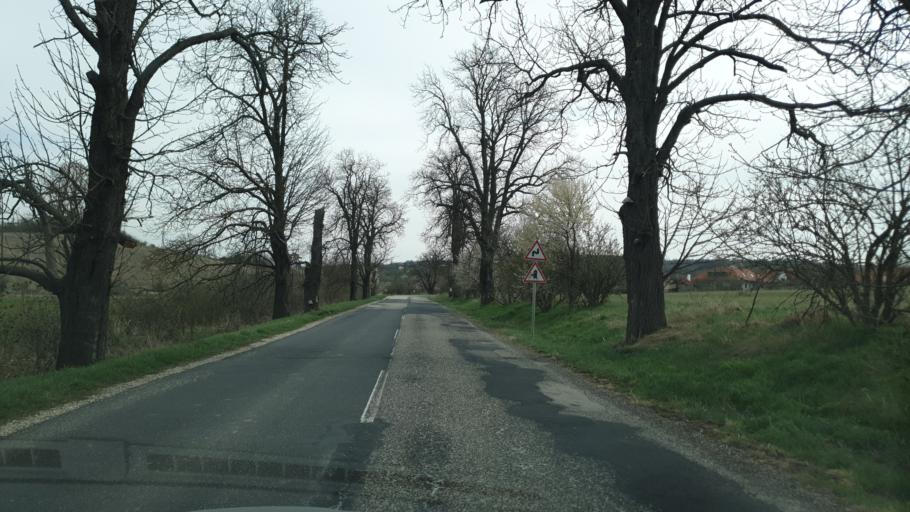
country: HU
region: Fejer
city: Etyek
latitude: 47.4623
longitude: 18.7254
